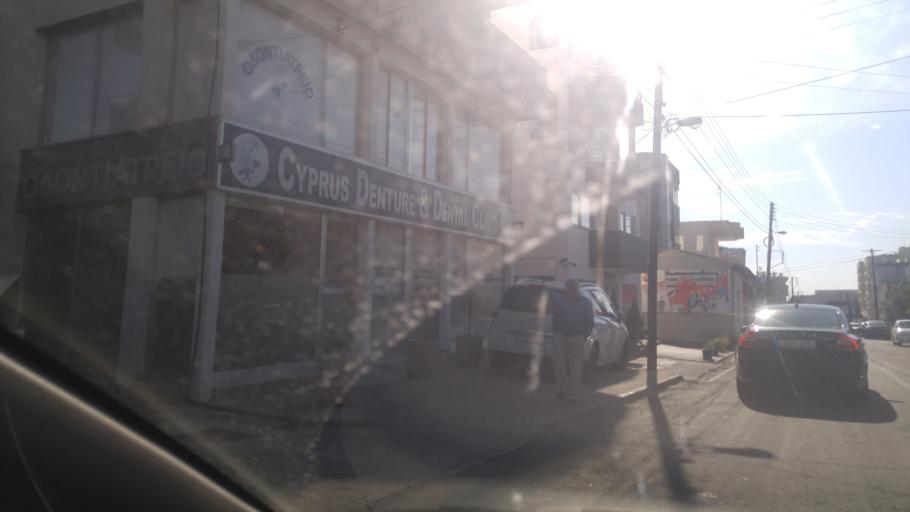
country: CY
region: Limassol
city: Limassol
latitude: 34.6894
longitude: 33.0541
